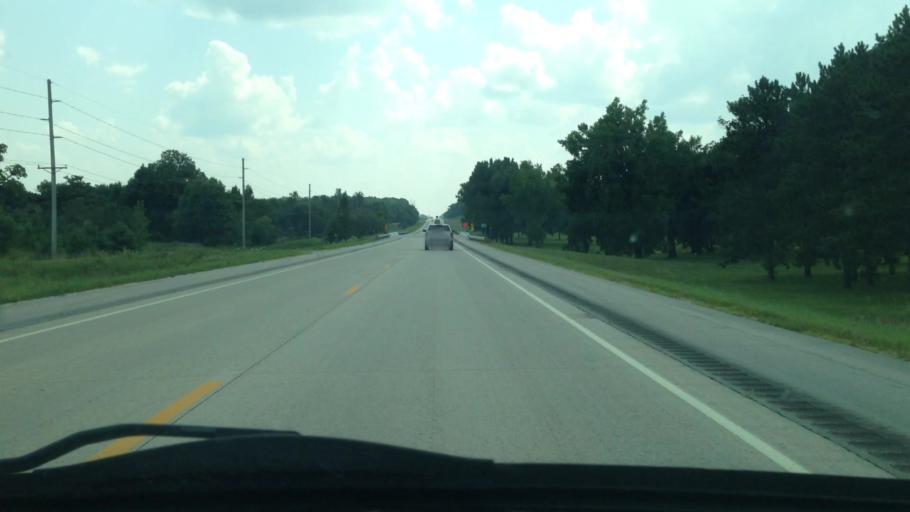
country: US
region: Minnesota
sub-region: Fillmore County
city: Spring Valley
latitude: 43.6284
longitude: -92.3895
